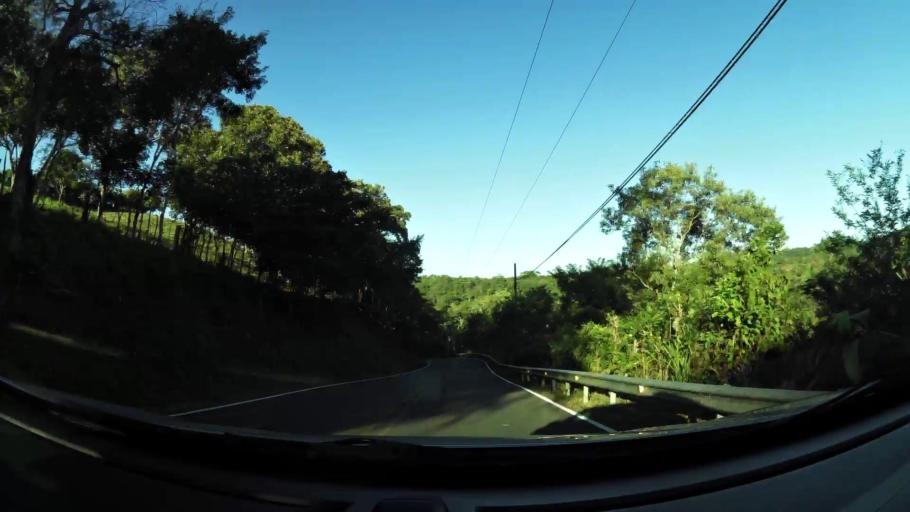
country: CR
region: Puntarenas
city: Miramar
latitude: 10.1263
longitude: -84.8308
